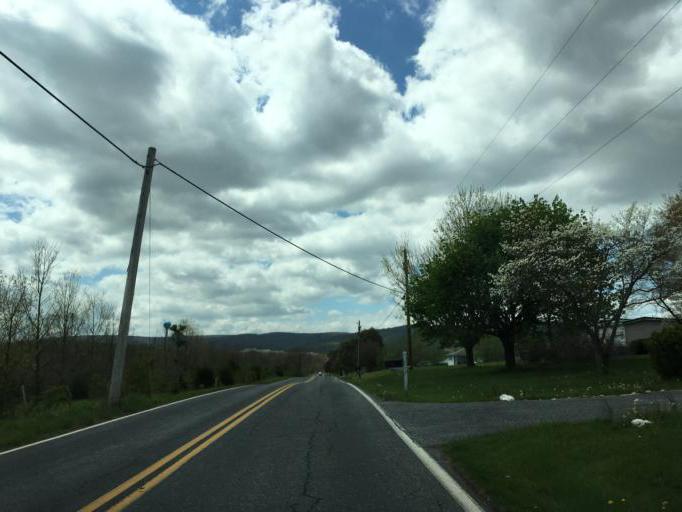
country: US
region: Maryland
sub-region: Frederick County
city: Thurmont
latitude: 39.6282
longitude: -77.3831
